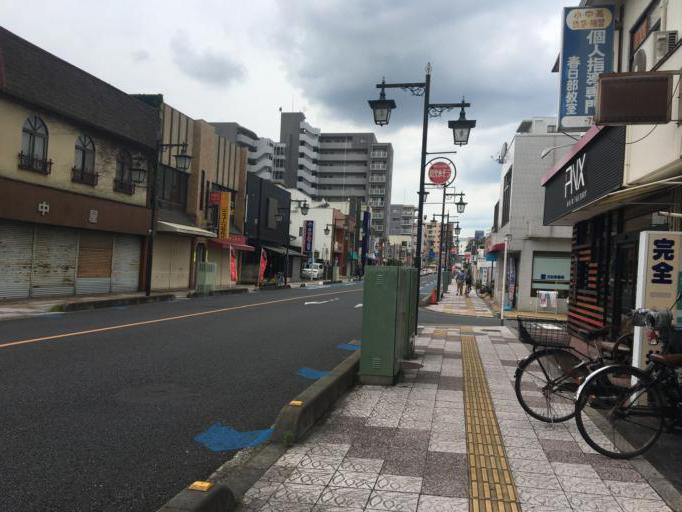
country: JP
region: Saitama
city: Kasukabe
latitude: 35.9818
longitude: 139.7566
